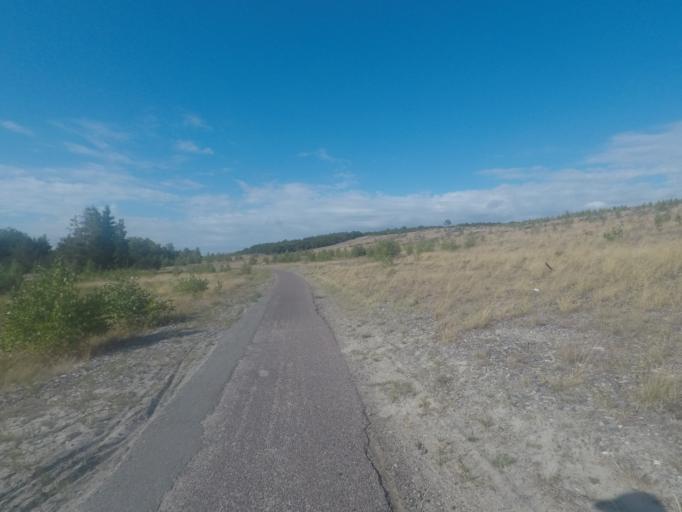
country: LT
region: Klaipedos apskritis
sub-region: Klaipeda
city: Klaipeda
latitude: 55.5954
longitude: 21.1155
